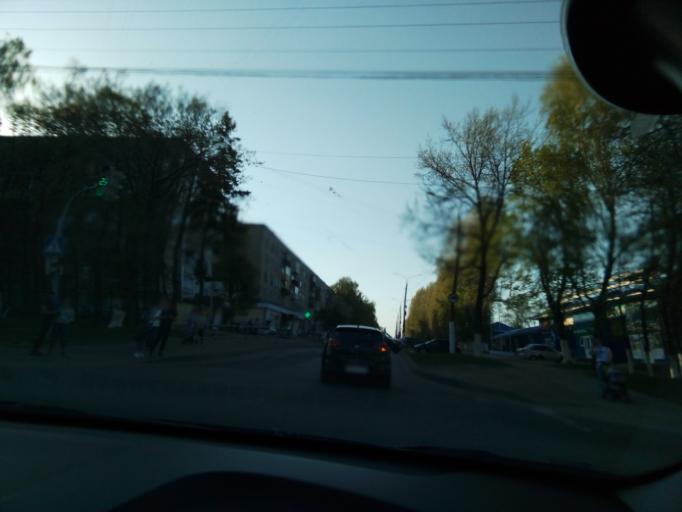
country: RU
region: Chuvashia
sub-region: Cheboksarskiy Rayon
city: Cheboksary
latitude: 56.1409
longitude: 47.1983
